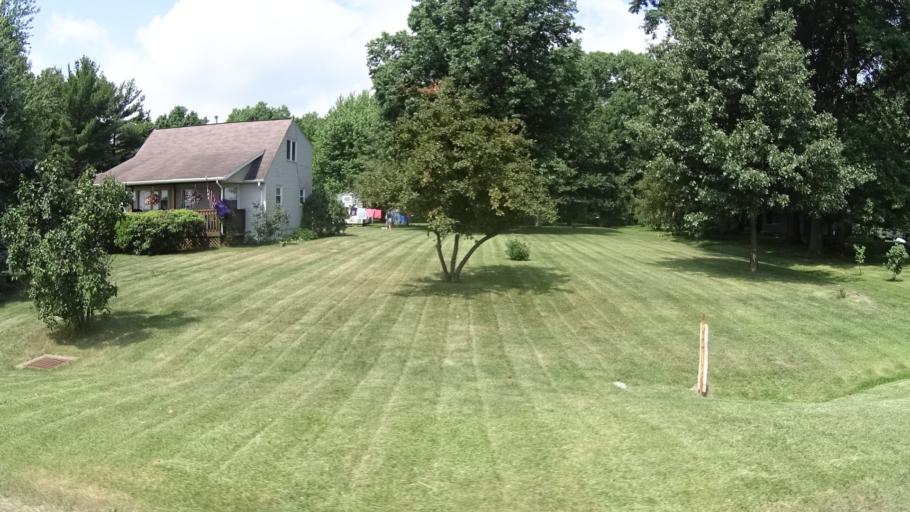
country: US
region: Ohio
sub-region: Lorain County
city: Vermilion
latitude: 41.3827
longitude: -82.3642
